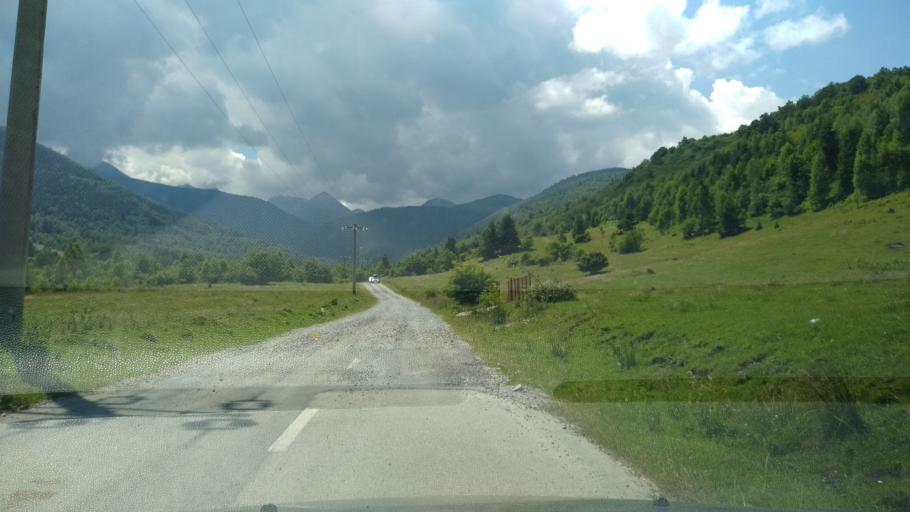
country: RO
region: Hunedoara
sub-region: Comuna Rau de Mori
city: Rau de Mori
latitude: 45.4579
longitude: 22.8978
